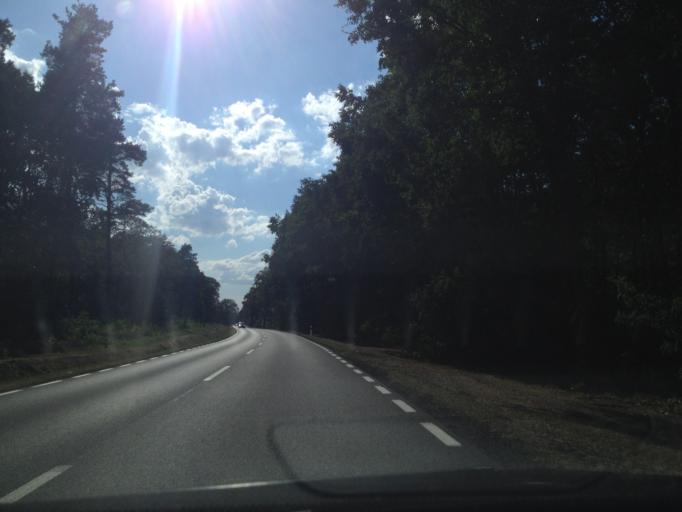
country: PL
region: Lubusz
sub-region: Powiat zarski
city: Tuplice
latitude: 51.6375
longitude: 14.9030
